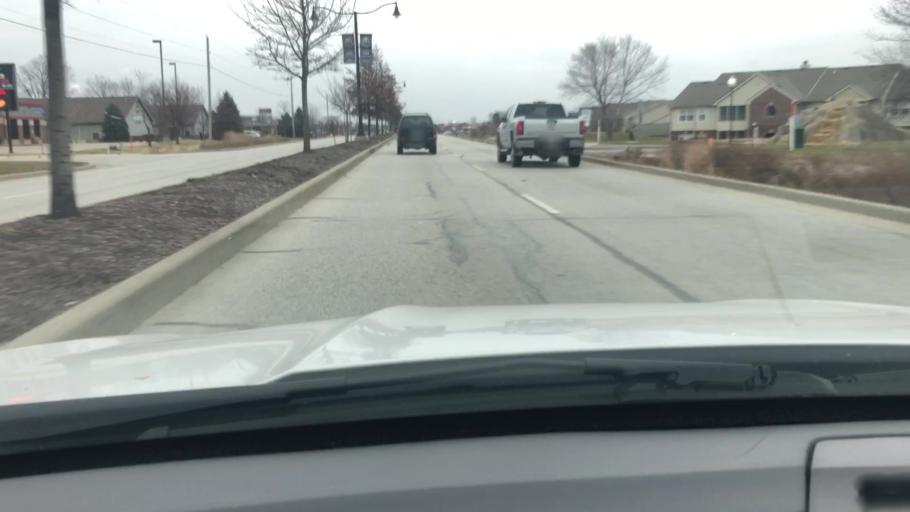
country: US
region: Indiana
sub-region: Tippecanoe County
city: Lafayette
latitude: 40.3671
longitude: -86.8685
